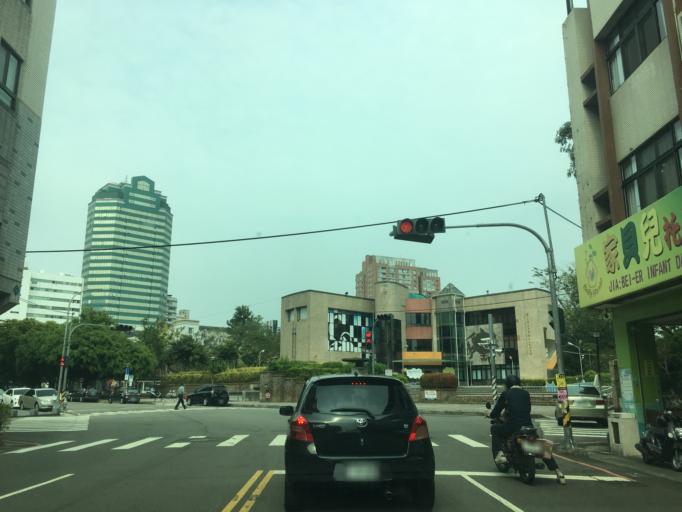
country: TW
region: Taiwan
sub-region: Taichung City
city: Taichung
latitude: 24.1689
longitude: 120.6938
